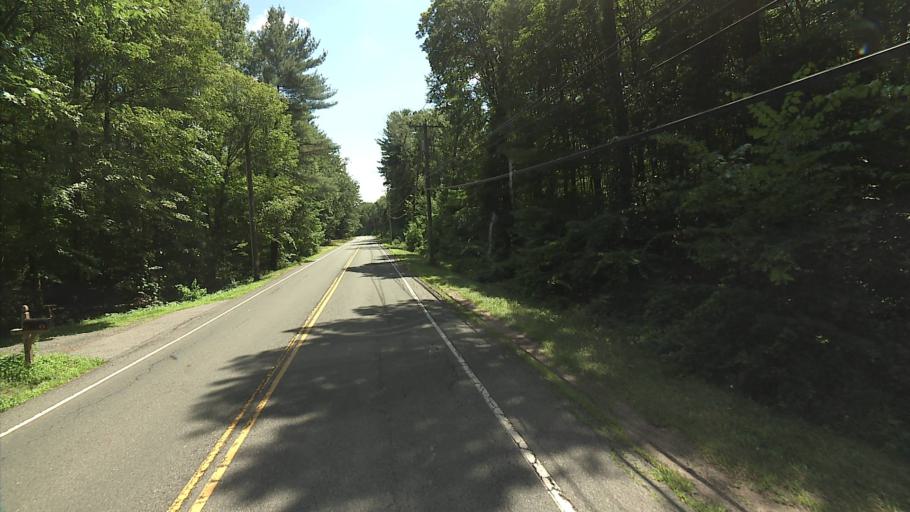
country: US
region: Massachusetts
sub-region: Hampden County
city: Southwick
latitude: 42.0033
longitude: -72.7254
